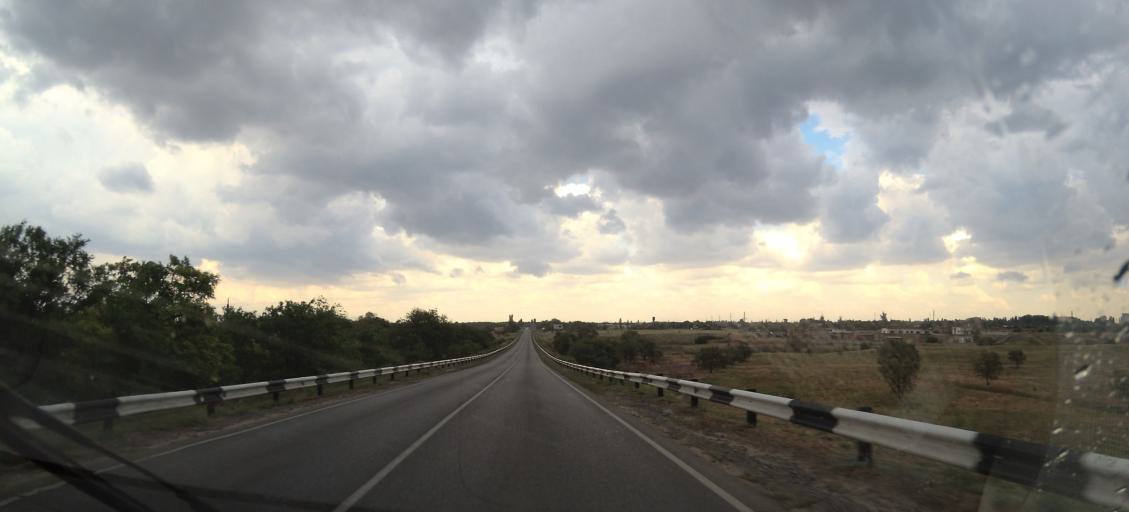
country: RU
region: Rostov
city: Orlovskiy
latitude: 46.8827
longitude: 42.0264
